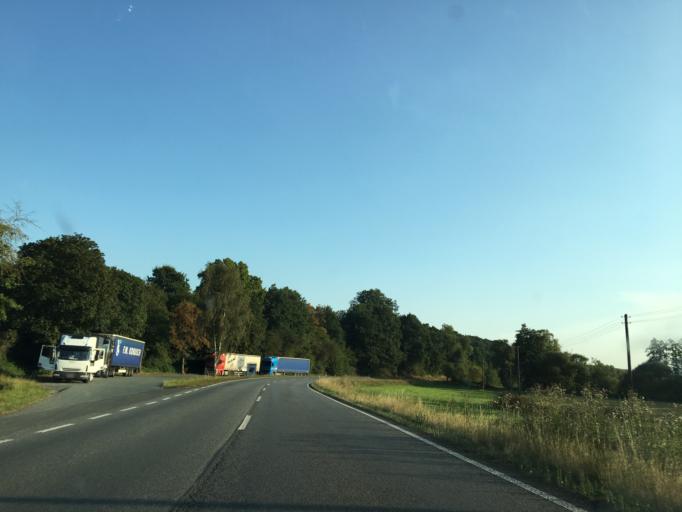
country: DE
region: Hesse
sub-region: Regierungsbezirk Giessen
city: Munchhausen
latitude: 50.9543
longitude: 8.7150
